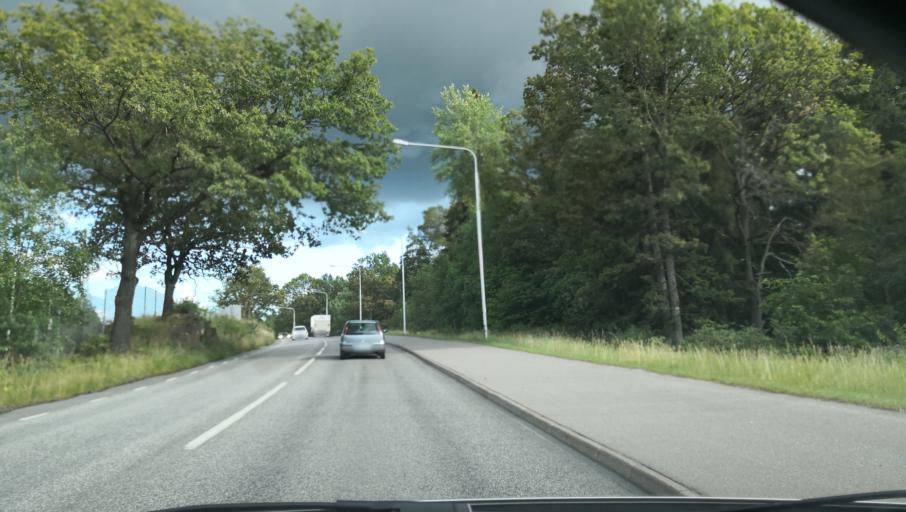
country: SE
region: Stockholm
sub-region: Stockholms Kommun
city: Arsta
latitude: 59.2458
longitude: 18.0680
